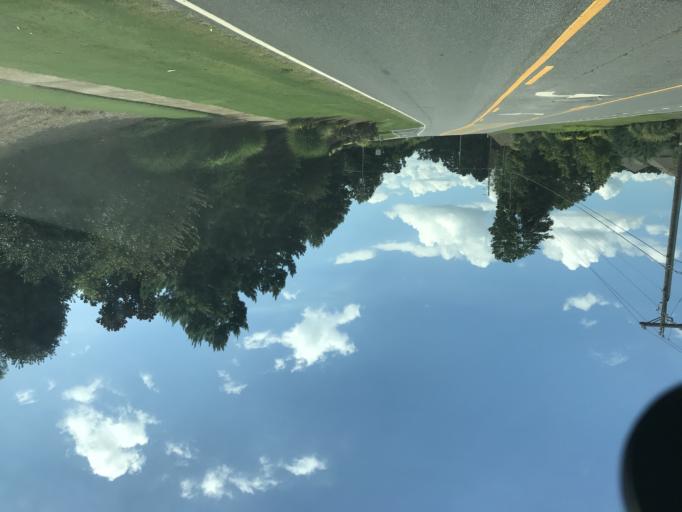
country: US
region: Georgia
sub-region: Forsyth County
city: Cumming
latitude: 34.2286
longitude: -84.2428
